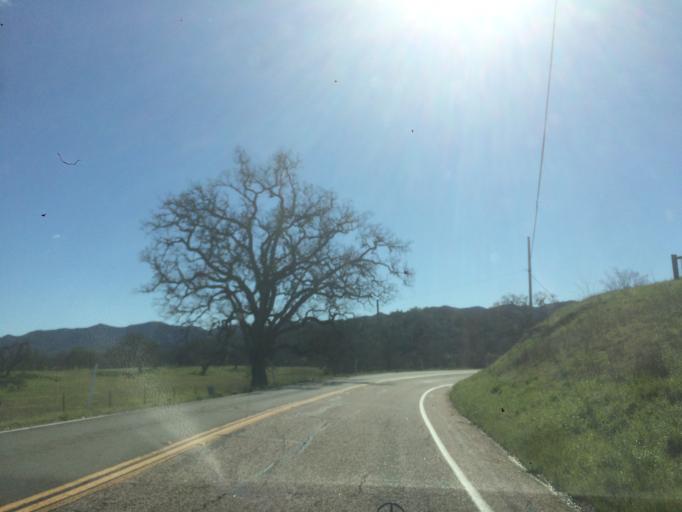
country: US
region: California
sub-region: San Luis Obispo County
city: Santa Margarita
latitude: 35.3915
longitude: -120.5771
